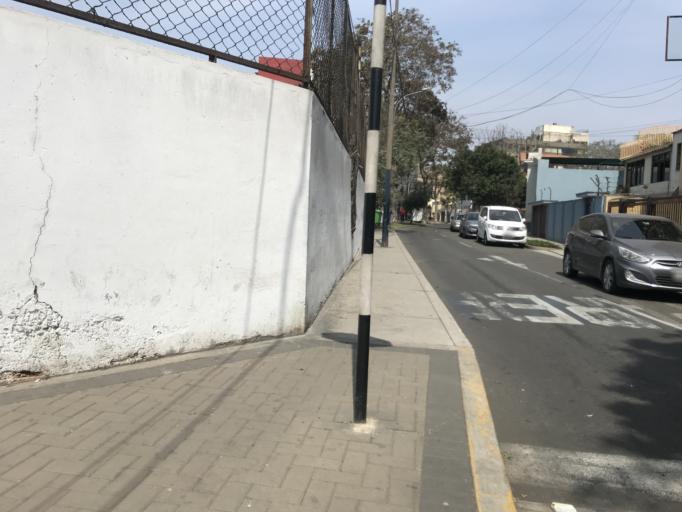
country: PE
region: Lima
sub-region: Lima
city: San Isidro
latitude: -12.1018
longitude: -77.0337
